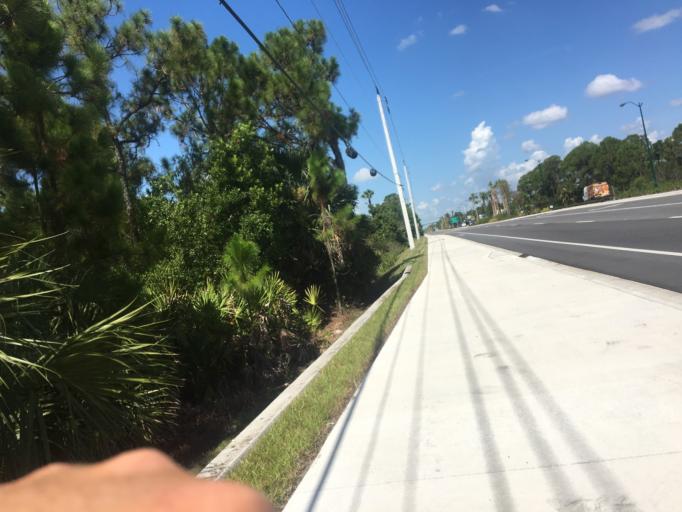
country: US
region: Florida
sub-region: Martin County
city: Palm City
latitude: 27.1611
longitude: -80.2717
